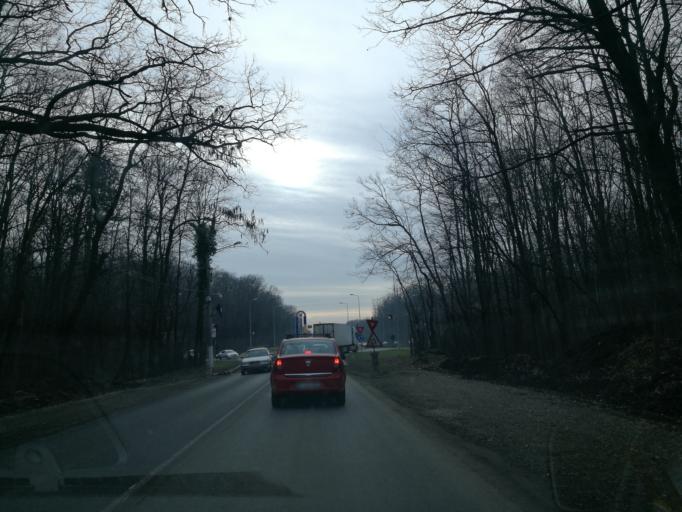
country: RO
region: Ilfov
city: Stefanestii de Jos
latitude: 44.5161
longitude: 26.1911
